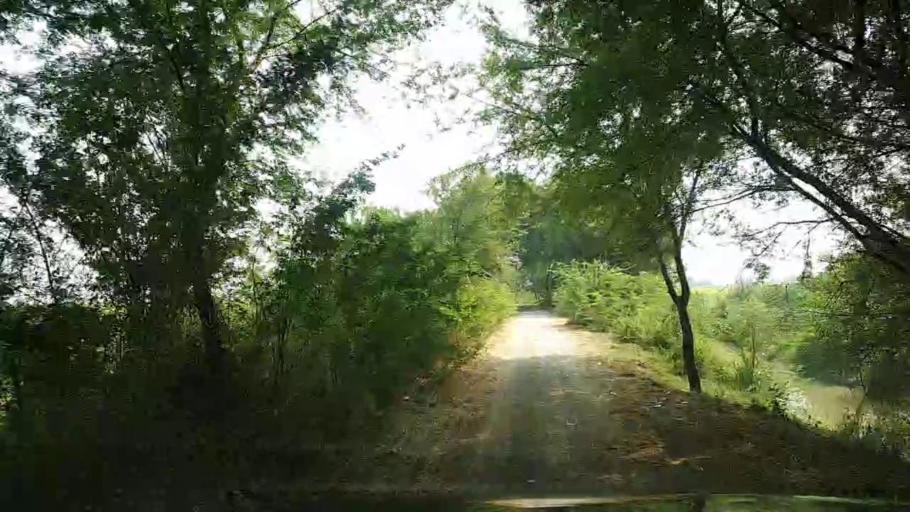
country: PK
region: Sindh
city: Mirpur Batoro
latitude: 24.6896
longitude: 68.2212
